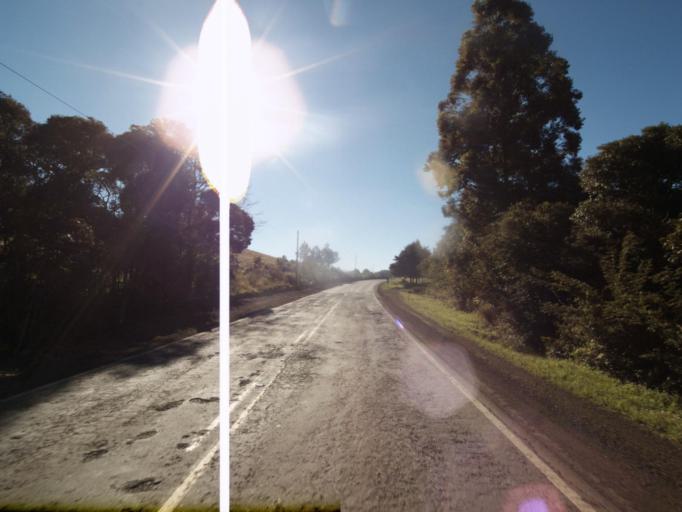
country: AR
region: Misiones
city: Bernardo de Irigoyen
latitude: -26.6191
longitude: -53.5185
